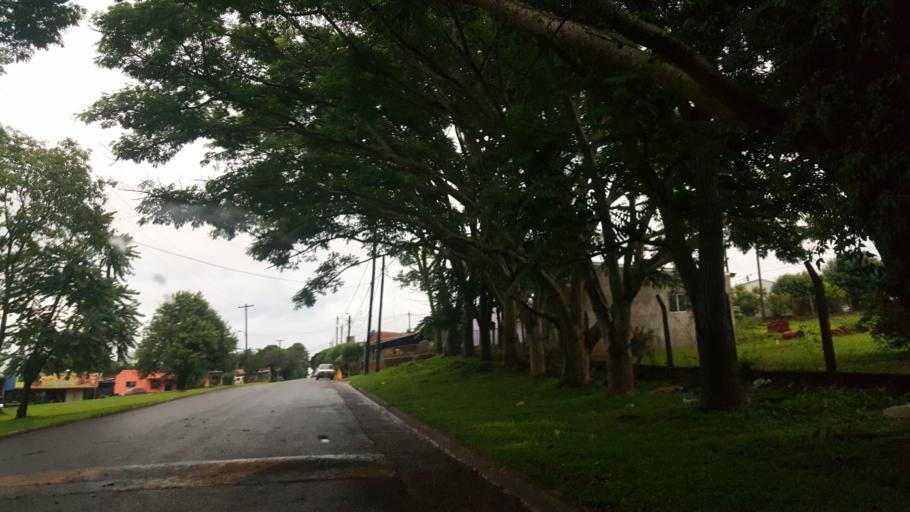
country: AR
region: Misiones
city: Santo Pipo
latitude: -27.1383
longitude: -55.4100
